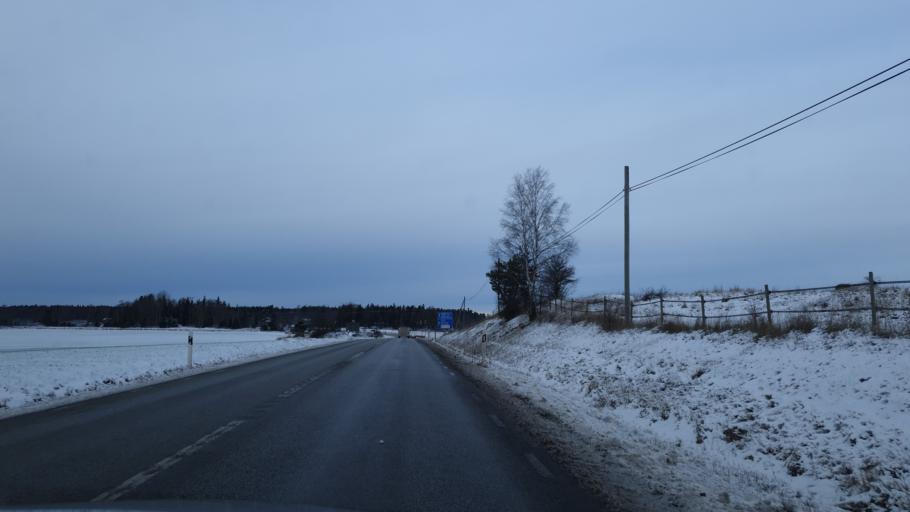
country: SE
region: Uppsala
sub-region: Habo Kommun
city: Balsta
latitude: 59.6263
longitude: 17.6027
